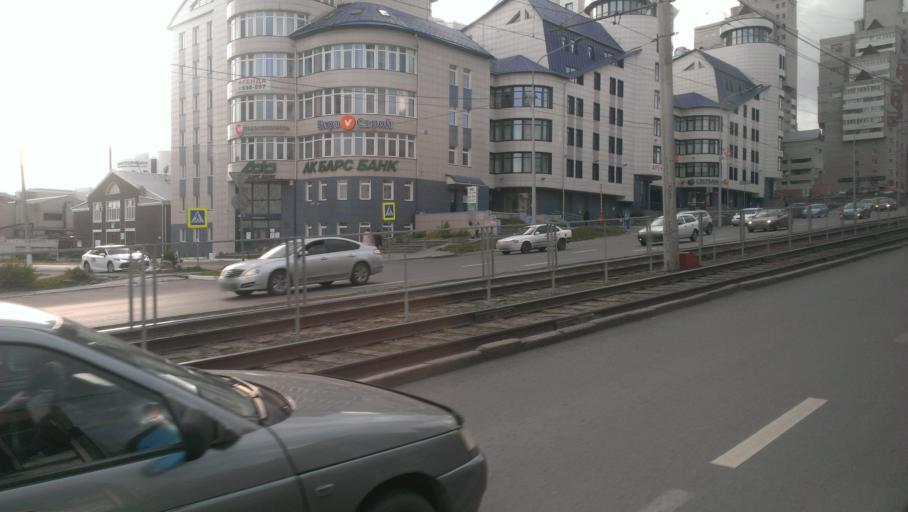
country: RU
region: Altai Krai
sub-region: Gorod Barnaulskiy
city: Barnaul
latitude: 53.3399
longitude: 83.7721
